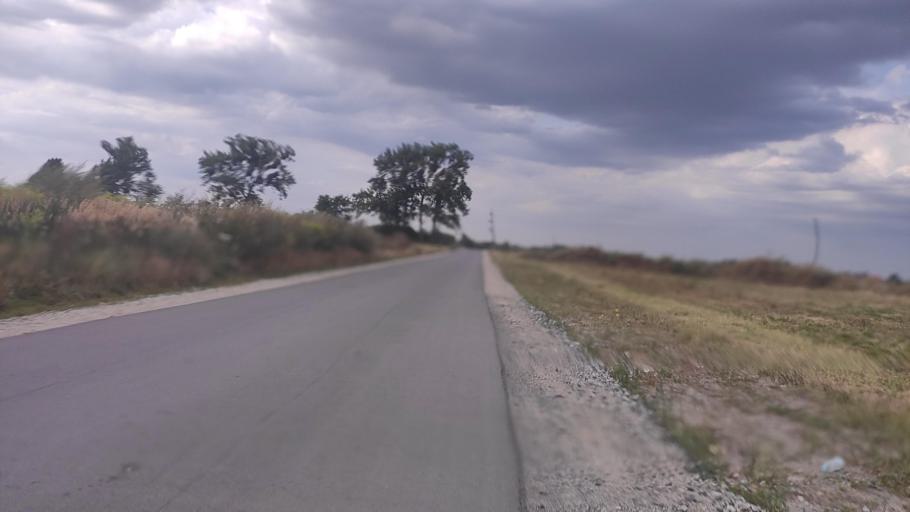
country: PL
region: Greater Poland Voivodeship
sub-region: Powiat poznanski
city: Swarzedz
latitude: 52.4155
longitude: 17.1021
